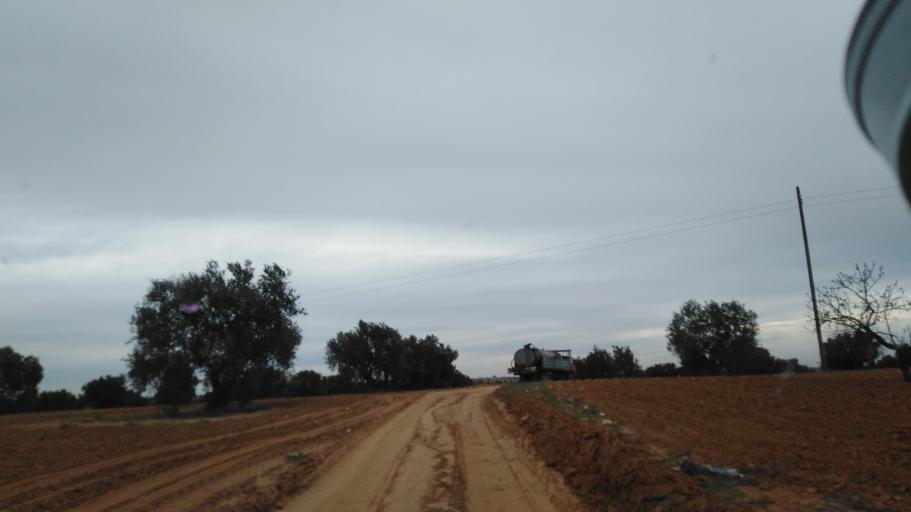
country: TN
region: Safaqis
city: Bi'r `Ali Bin Khalifah
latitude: 34.7717
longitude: 10.3735
